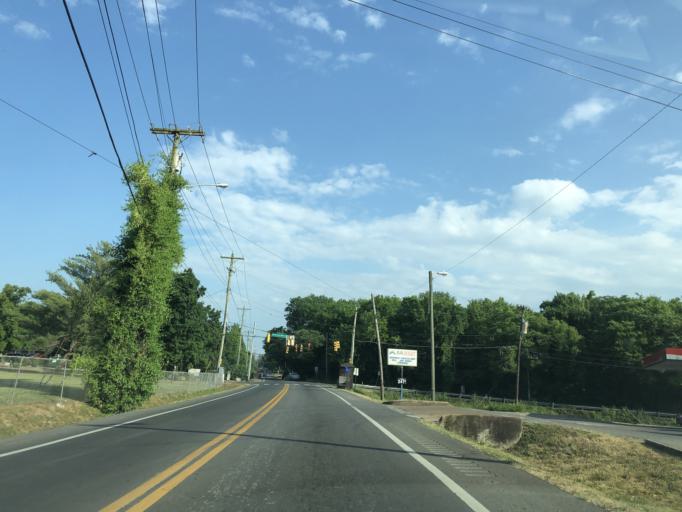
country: US
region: Tennessee
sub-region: Davidson County
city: Nashville
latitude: 36.2189
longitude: -86.8041
